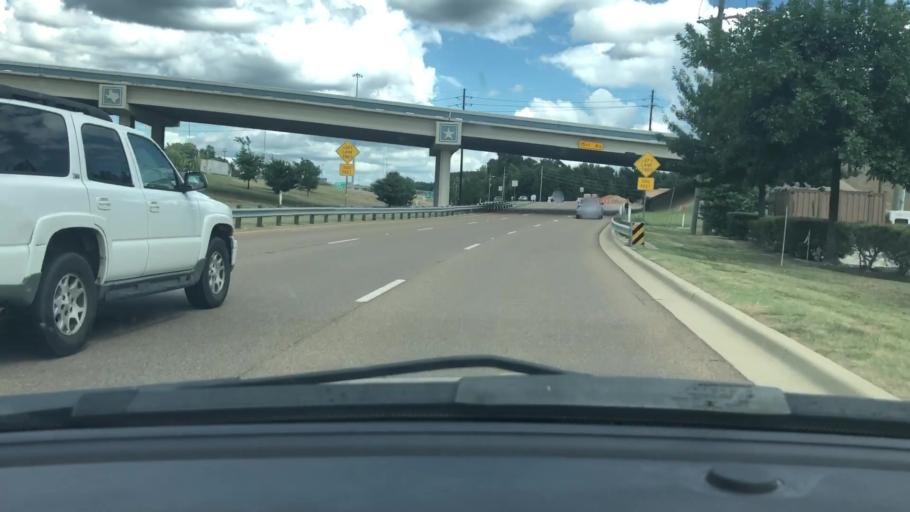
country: US
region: Texas
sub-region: Bowie County
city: Wake Village
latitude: 33.4600
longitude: -94.0776
